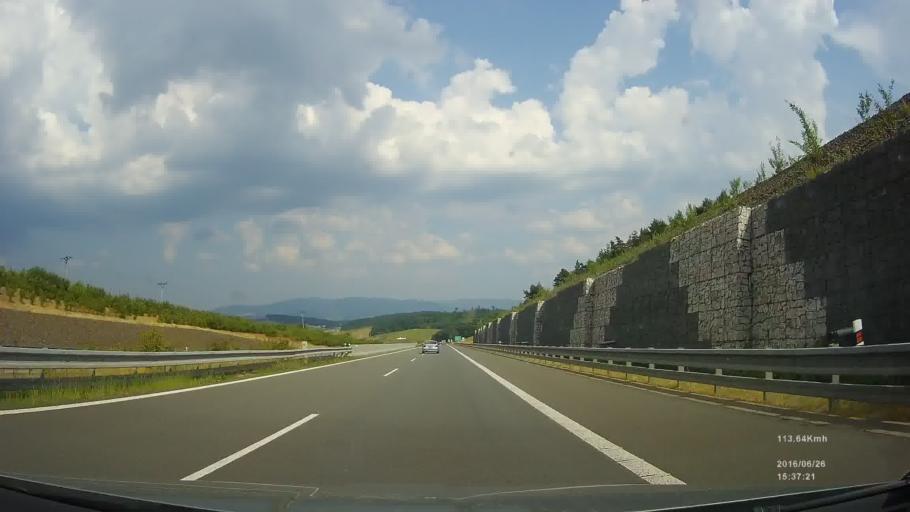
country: SK
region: Presovsky
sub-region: Okres Presov
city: Presov
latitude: 49.0050
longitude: 21.1522
